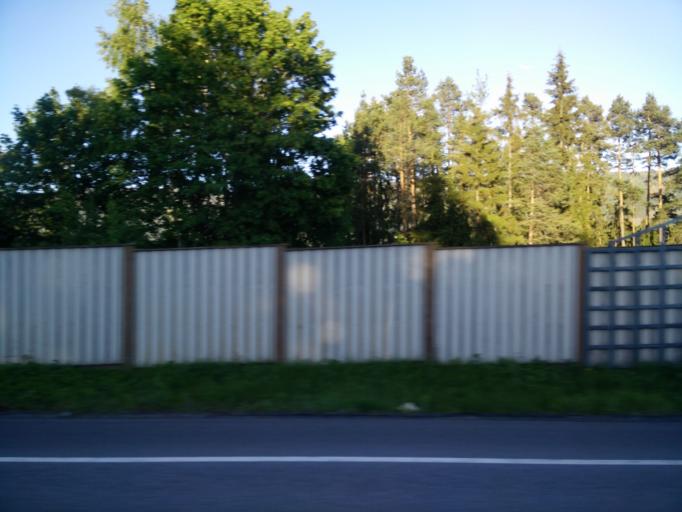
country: NO
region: Buskerud
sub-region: Hole
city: Vik
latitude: 60.0866
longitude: 10.2863
